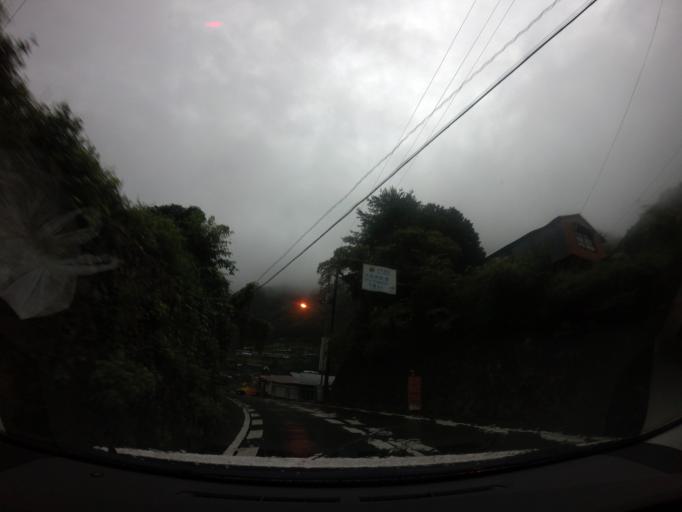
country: JP
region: Wakayama
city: Shingu
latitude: 33.9462
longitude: 135.8047
